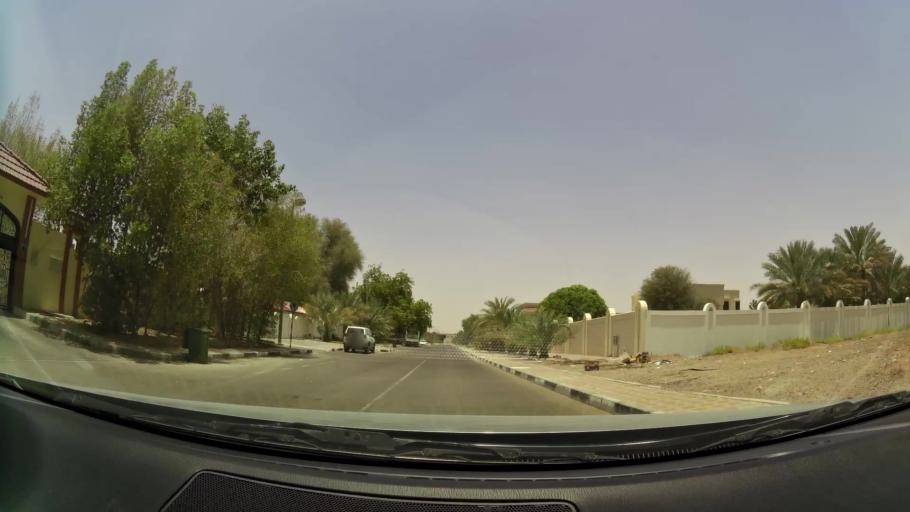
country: OM
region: Al Buraimi
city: Al Buraymi
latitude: 24.2802
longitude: 55.7365
